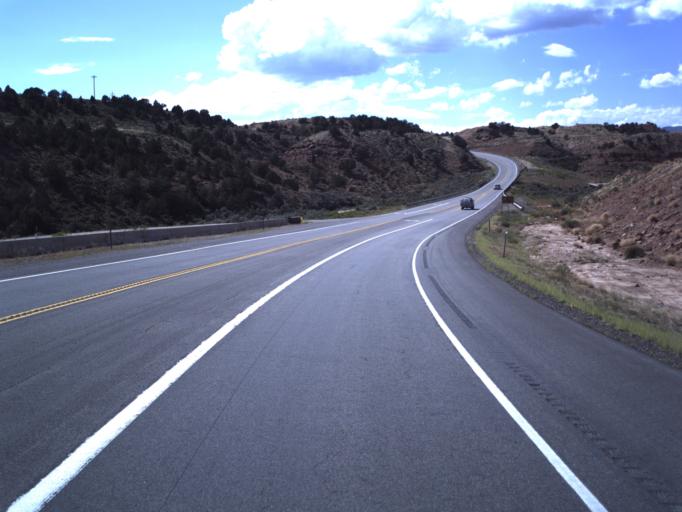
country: US
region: Utah
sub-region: Duchesne County
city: Duchesne
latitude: 40.1993
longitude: -110.7812
